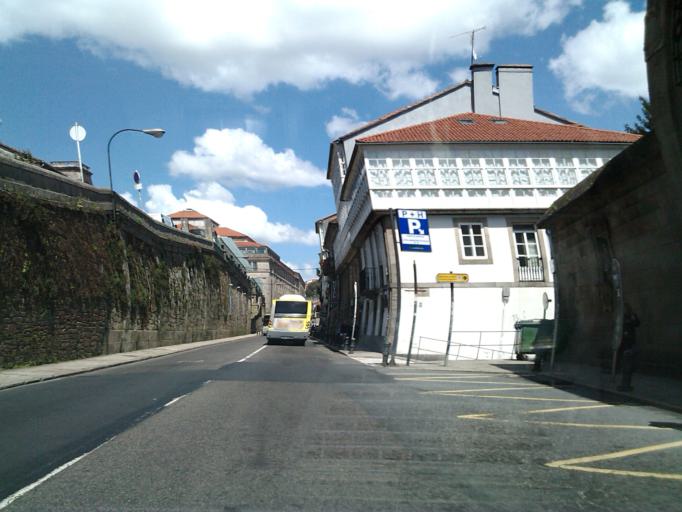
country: ES
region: Galicia
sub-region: Provincia da Coruna
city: Santiago de Compostela
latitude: 42.8789
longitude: -8.5412
